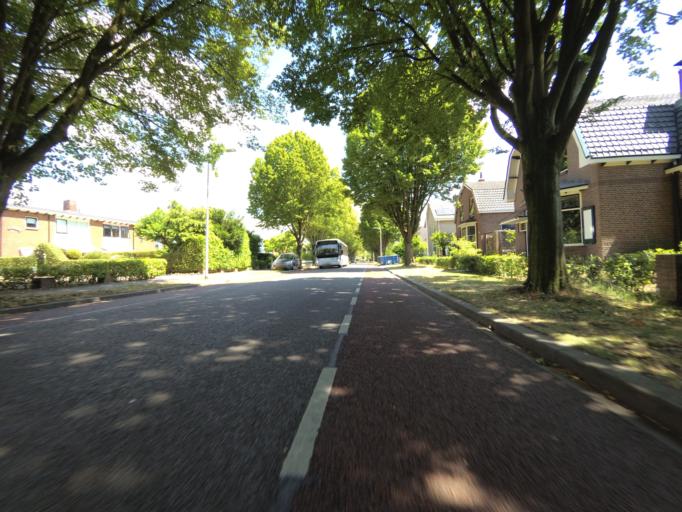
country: NL
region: Overijssel
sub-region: Gemeente Deventer
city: Schalkhaar
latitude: 52.2681
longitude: 6.1910
